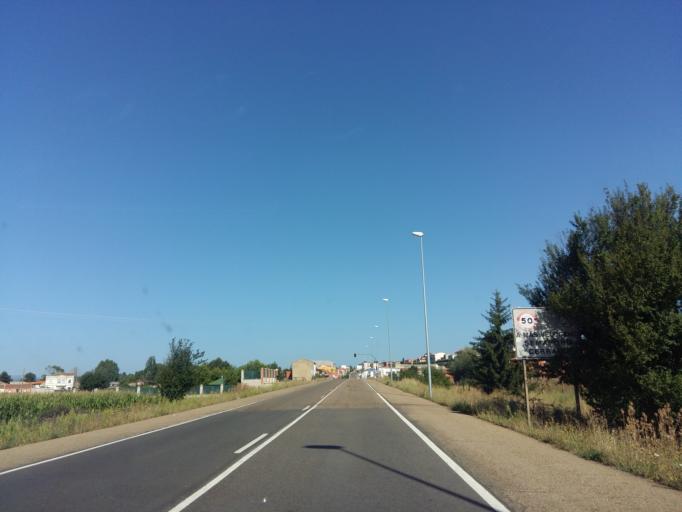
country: ES
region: Castille and Leon
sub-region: Provincia de Leon
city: Astorga
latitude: 42.4485
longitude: -6.0499
